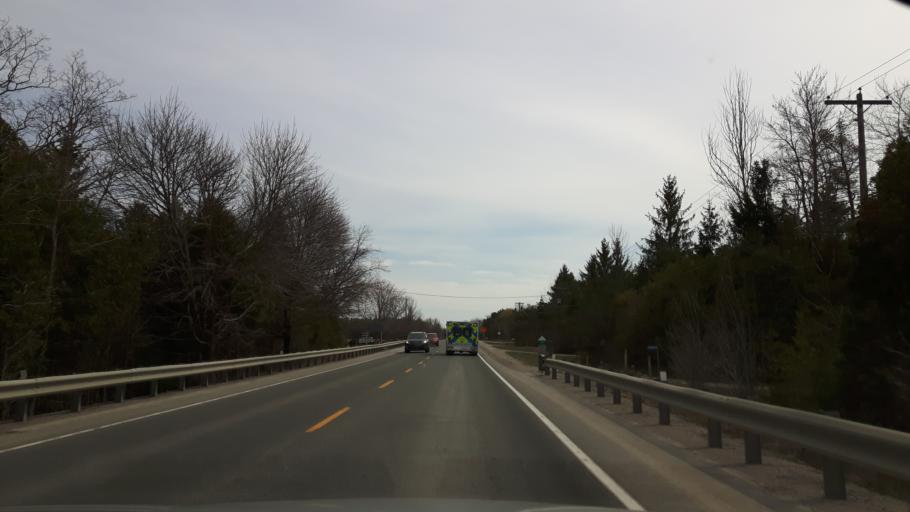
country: CA
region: Ontario
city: Bluewater
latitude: 43.5823
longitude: -81.7056
